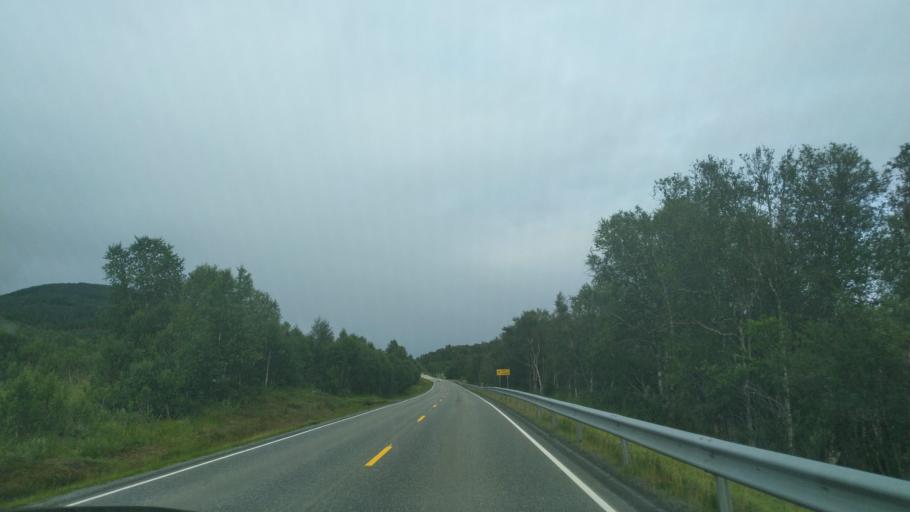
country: NO
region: Nordland
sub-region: Evenes
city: Randa
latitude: 68.4991
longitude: 16.8407
